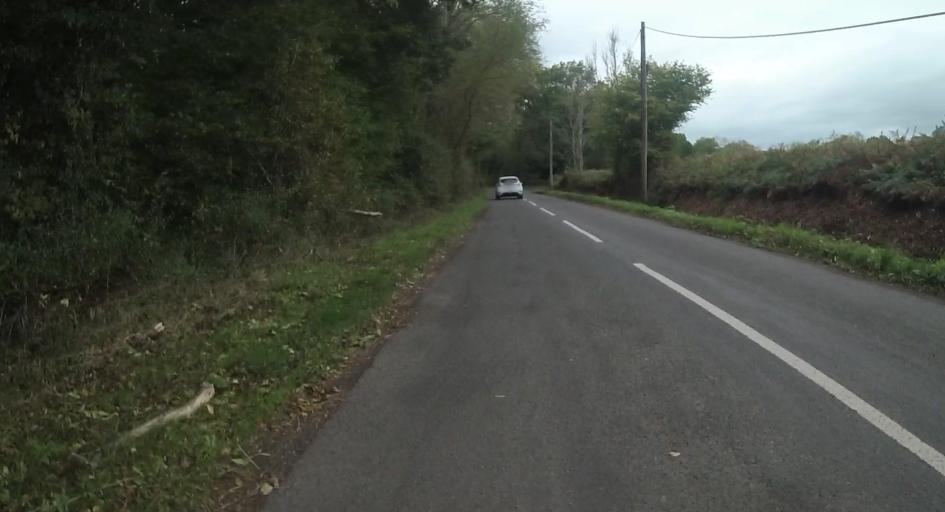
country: GB
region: England
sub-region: Hampshire
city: Odiham
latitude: 51.2806
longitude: -0.8988
